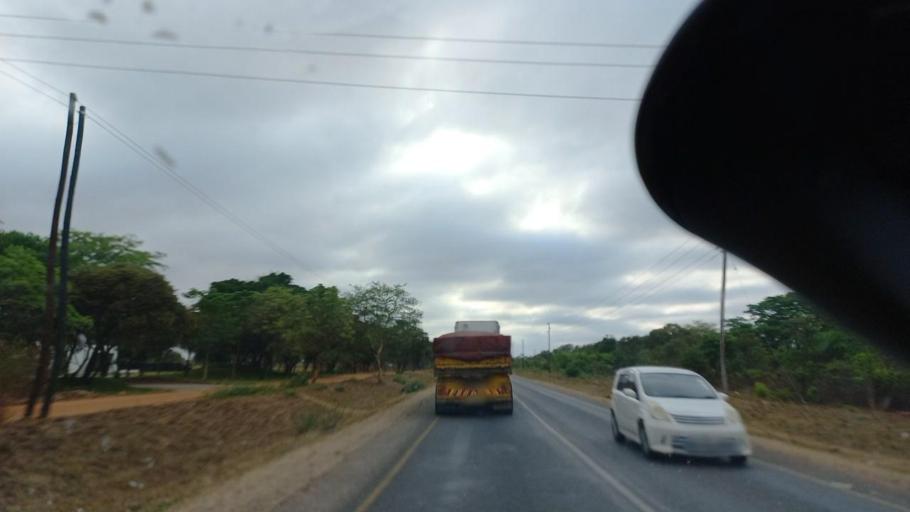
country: ZM
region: Lusaka
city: Chongwe
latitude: -15.3525
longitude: 28.5423
